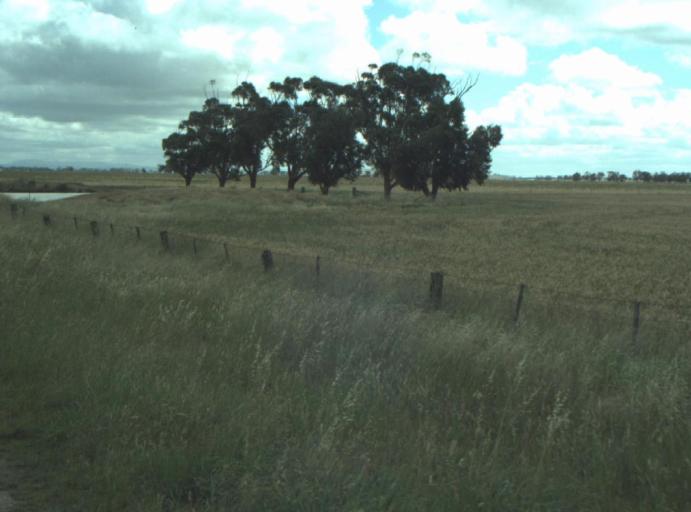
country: AU
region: Victoria
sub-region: Moorabool
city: Bacchus Marsh
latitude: -37.8350
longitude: 144.3565
